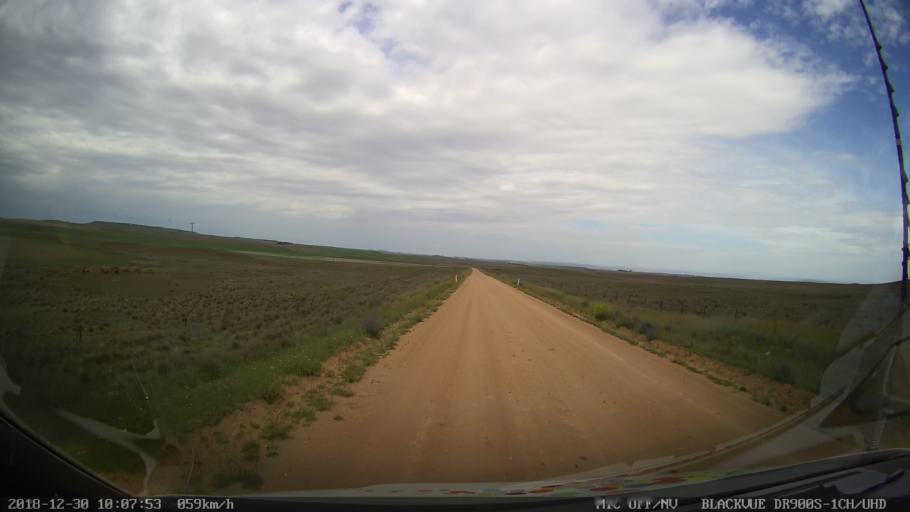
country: AU
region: New South Wales
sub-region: Cooma-Monaro
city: Cooma
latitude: -36.5418
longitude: 149.1189
